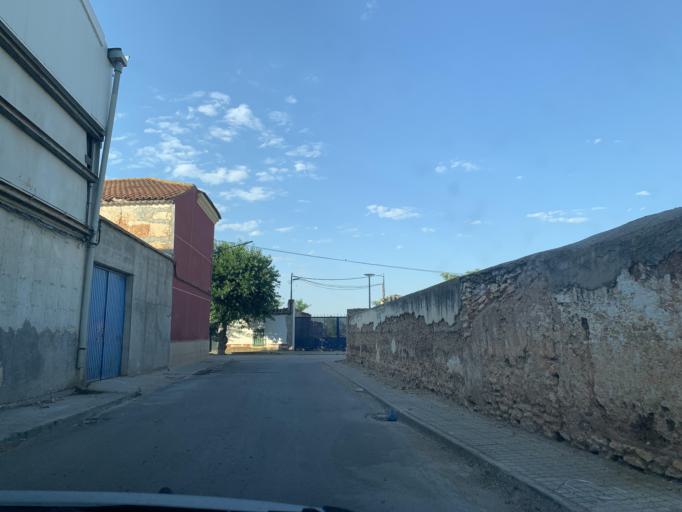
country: ES
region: Castille-La Mancha
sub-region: Provincia de Ciudad Real
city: Argamasilla de Alba
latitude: 39.1688
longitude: -3.2301
